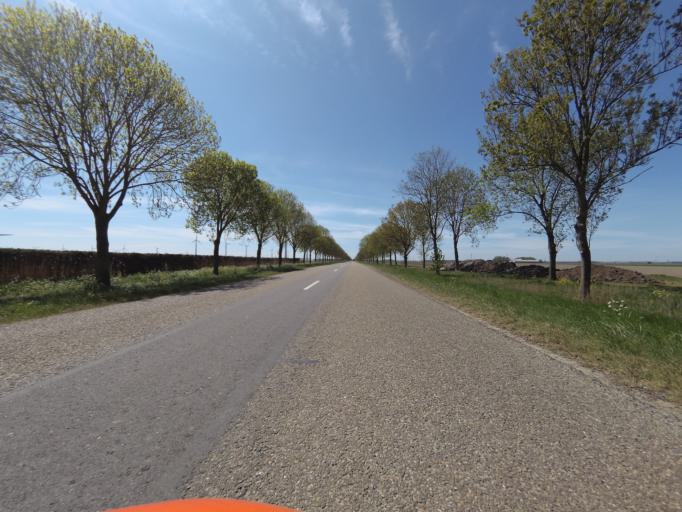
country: NL
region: Flevoland
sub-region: Gemeente Zeewolde
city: Zeewolde
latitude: 52.3486
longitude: 5.4493
